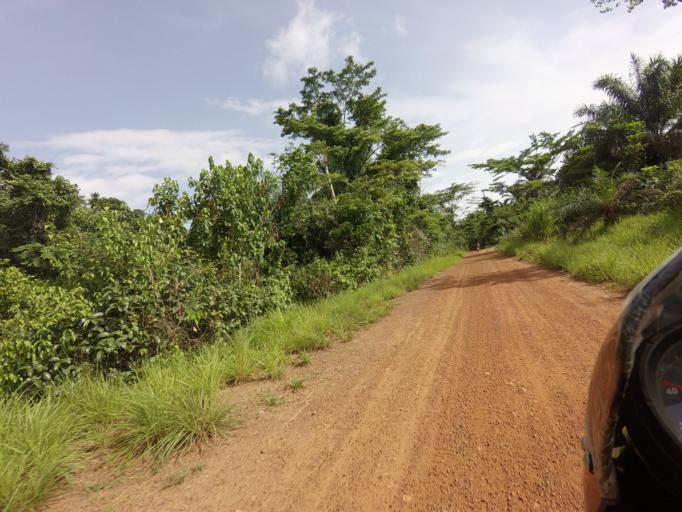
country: SL
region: Eastern Province
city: Jojoima
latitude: 7.8355
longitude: -10.8103
